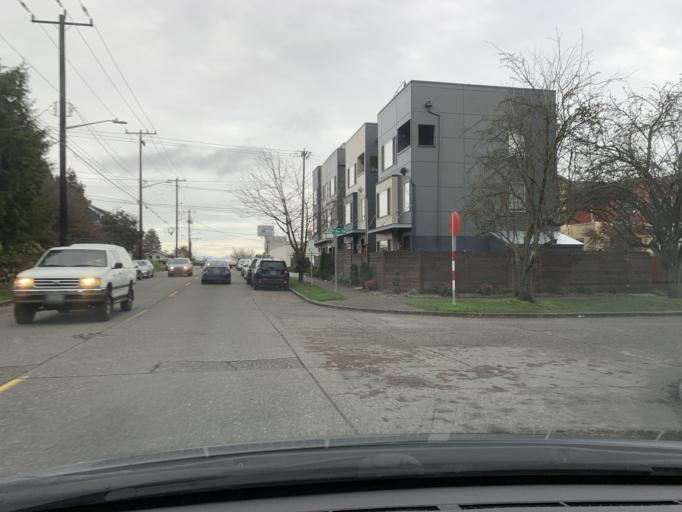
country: US
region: Washington
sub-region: King County
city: White Center
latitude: 47.5629
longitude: -122.3830
